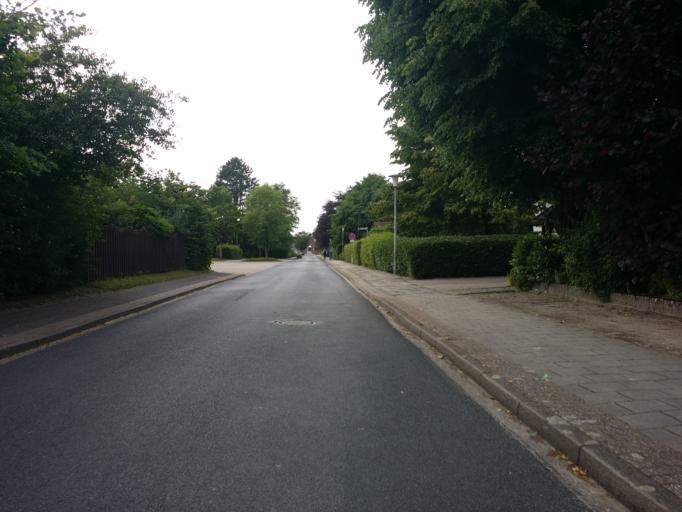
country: DE
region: Lower Saxony
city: Zetel
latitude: 53.3840
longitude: 7.9576
